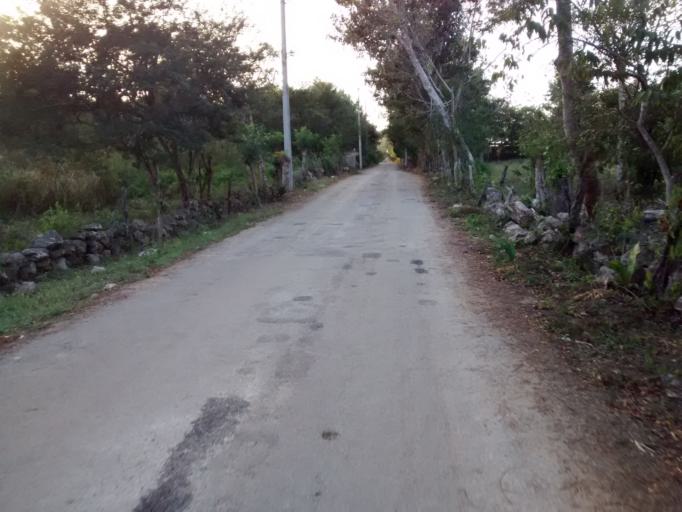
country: MX
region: Yucatan
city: Valladolid
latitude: 20.6805
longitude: -88.1601
